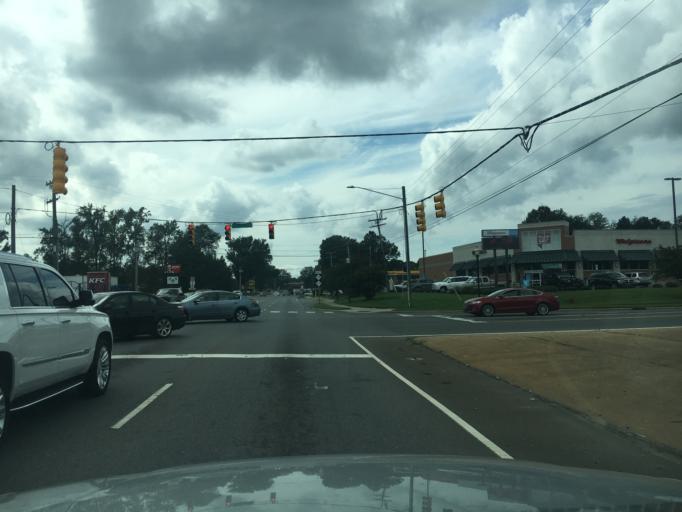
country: US
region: North Carolina
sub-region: Gaston County
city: Dallas
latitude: 35.3159
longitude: -81.1892
